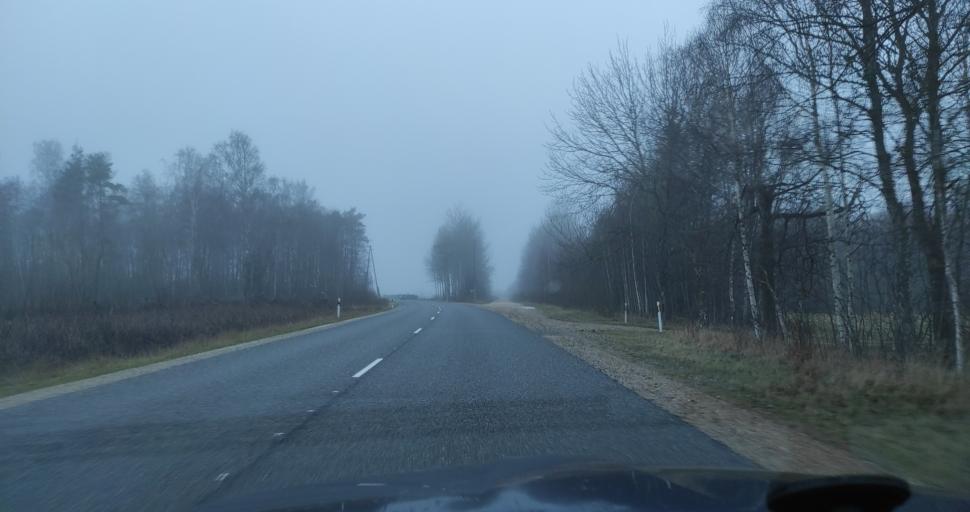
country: LV
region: Alsunga
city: Alsunga
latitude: 56.9945
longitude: 21.3704
